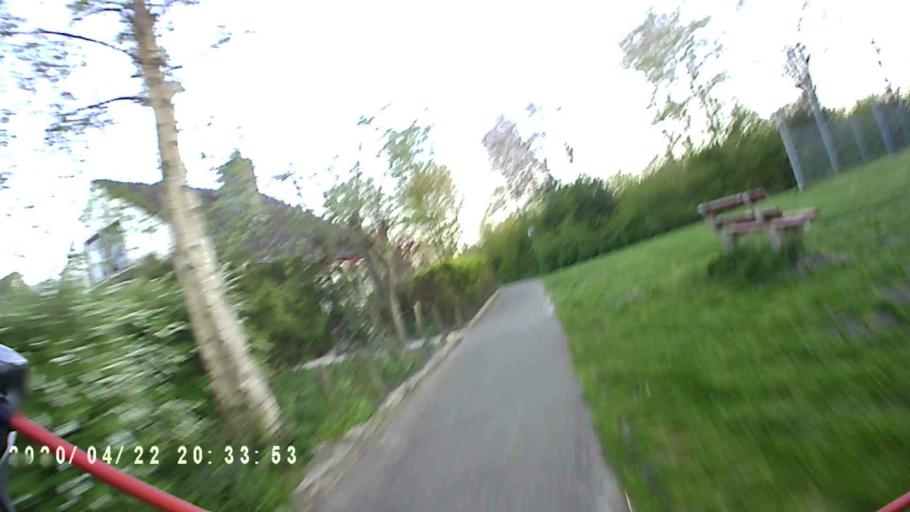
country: NL
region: Groningen
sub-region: Gemeente Winsum
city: Winsum
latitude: 53.3254
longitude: 6.5235
